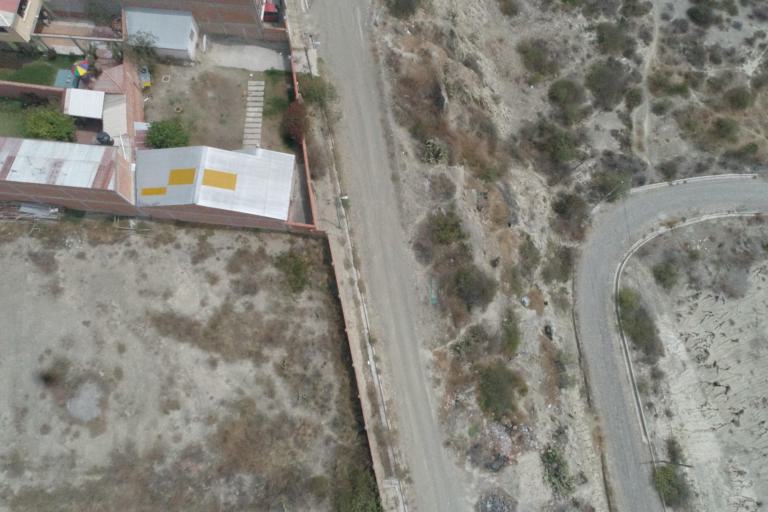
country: BO
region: La Paz
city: La Paz
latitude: -16.5993
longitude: -68.0704
